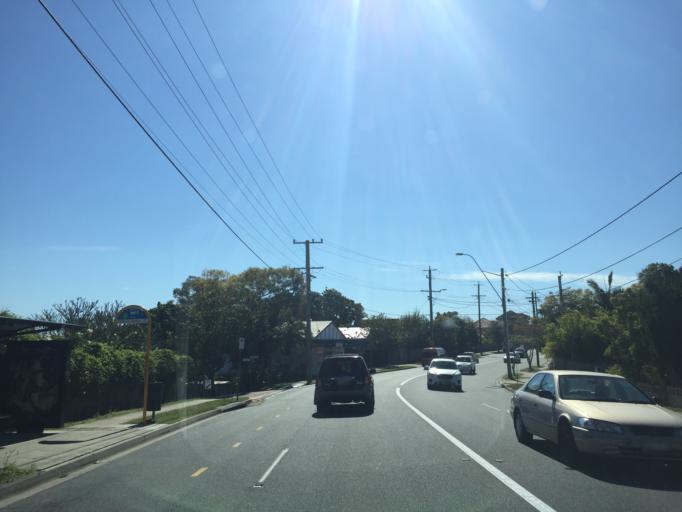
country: AU
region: Queensland
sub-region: Brisbane
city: Milton
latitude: -27.4468
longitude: 152.9846
